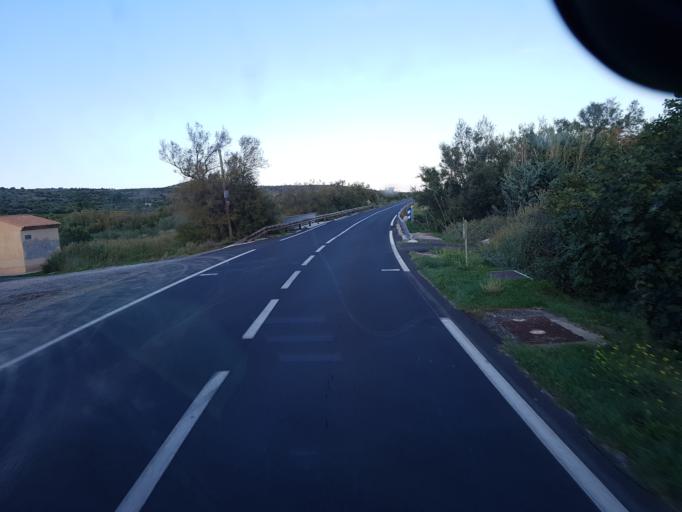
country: FR
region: Languedoc-Roussillon
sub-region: Departement de l'Aude
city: Sigean
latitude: 42.9738
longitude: 3.0022
